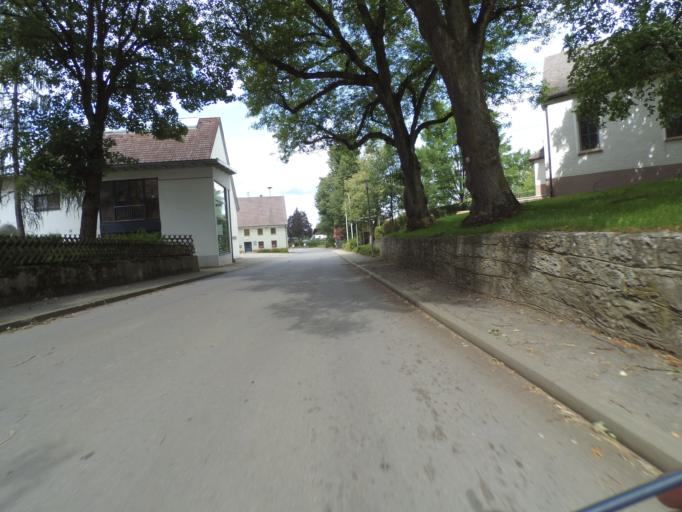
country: DE
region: Baden-Wuerttemberg
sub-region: Freiburg Region
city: Hufingen
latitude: 47.9082
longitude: 8.5392
